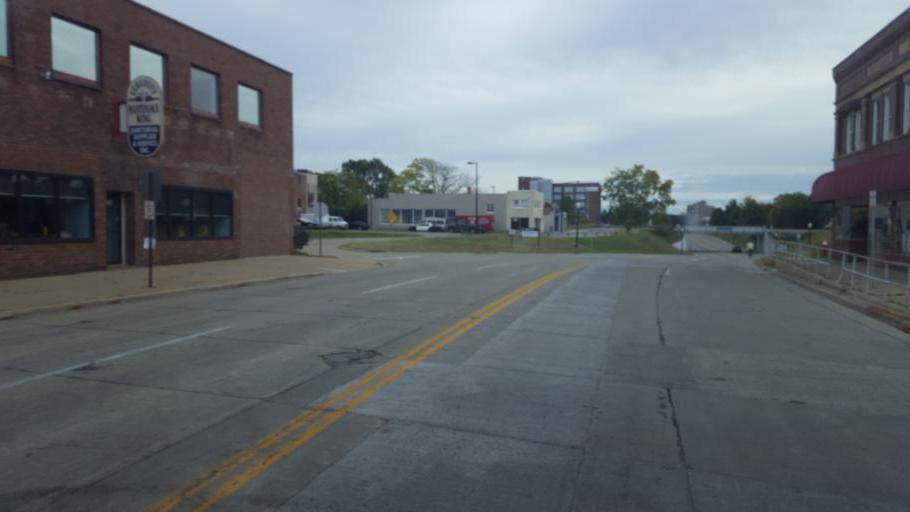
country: US
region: Ohio
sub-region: Lorain County
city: Lorain
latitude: 41.4627
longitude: -82.1725
